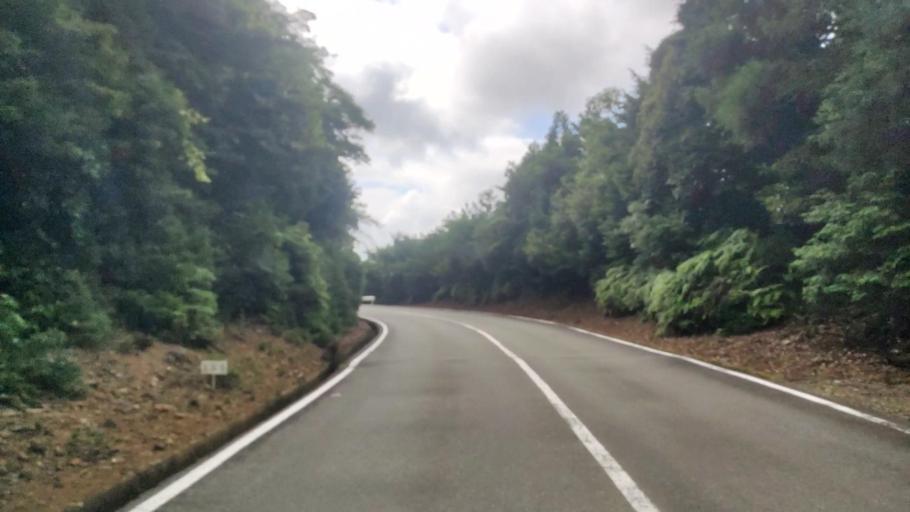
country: JP
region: Mie
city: Toba
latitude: 34.4583
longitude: 136.7786
